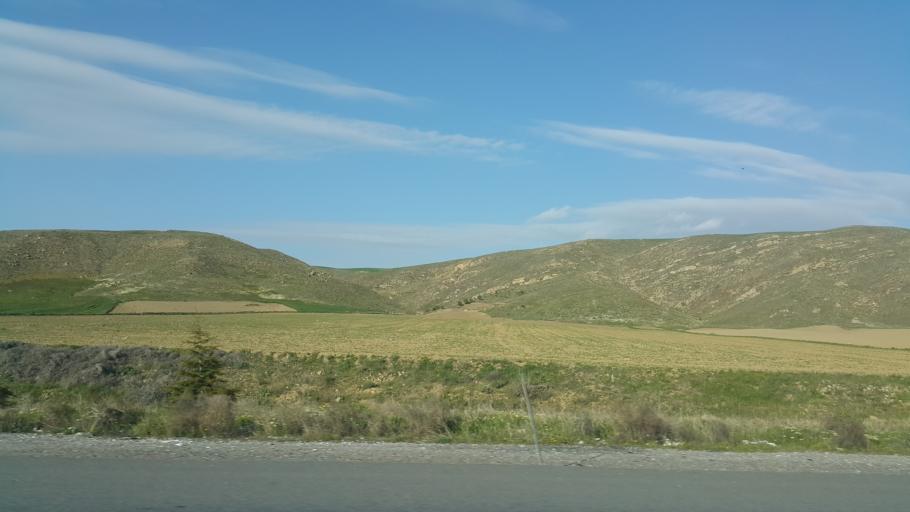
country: TR
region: Ankara
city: Sereflikochisar
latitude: 39.0511
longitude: 33.4354
